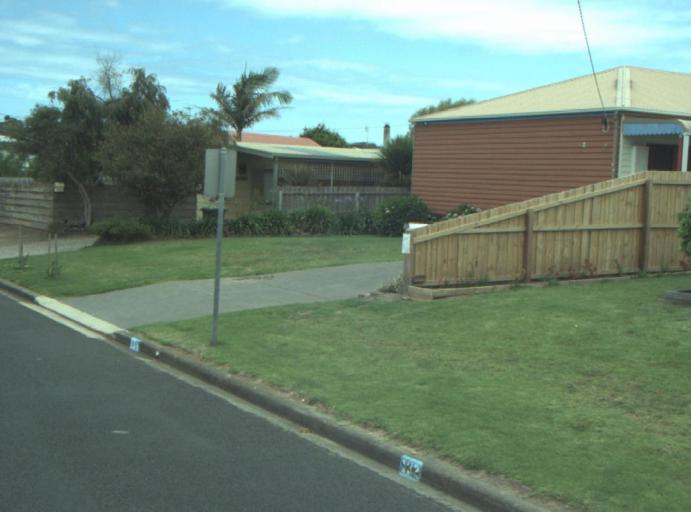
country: AU
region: Victoria
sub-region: Greater Geelong
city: Leopold
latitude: -38.2677
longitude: 144.5427
